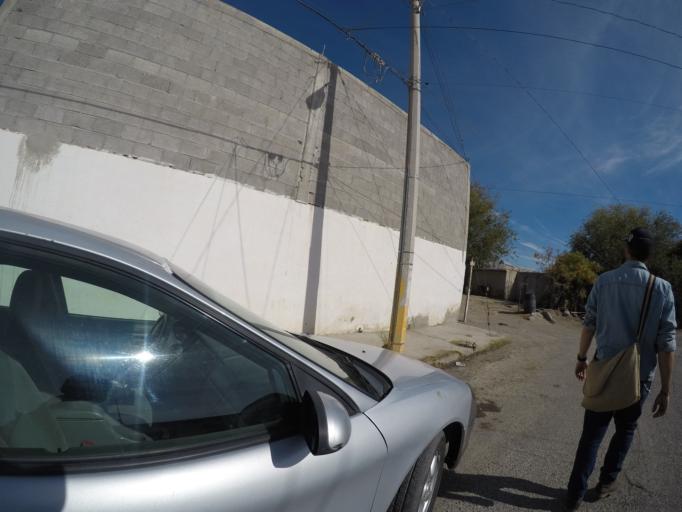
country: MX
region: Chihuahua
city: Ciudad Juarez
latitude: 31.7352
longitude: -106.4534
